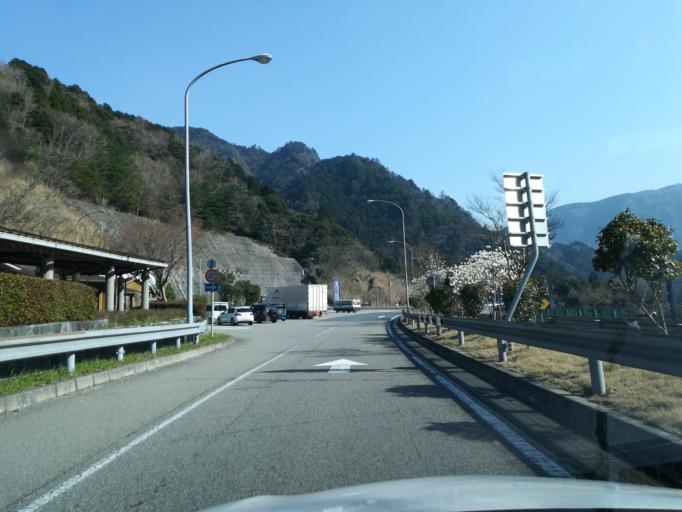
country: JP
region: Ehime
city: Kawanoecho
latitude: 33.9104
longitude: 133.6302
